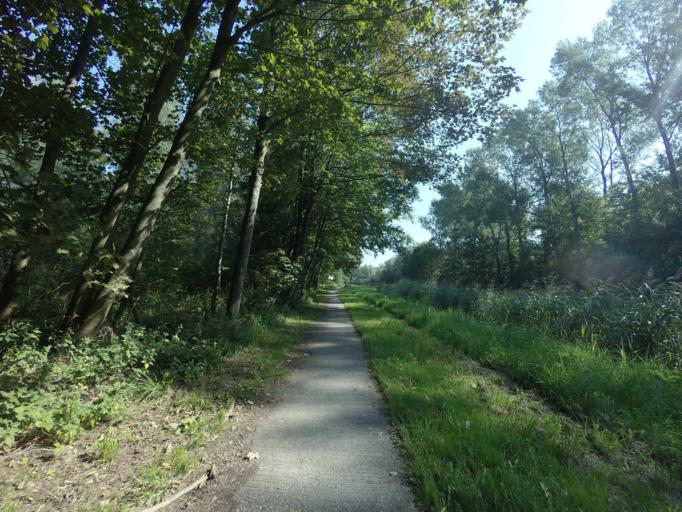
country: NL
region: Groningen
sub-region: Gemeente De Marne
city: Ulrum
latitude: 53.3907
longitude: 6.2606
